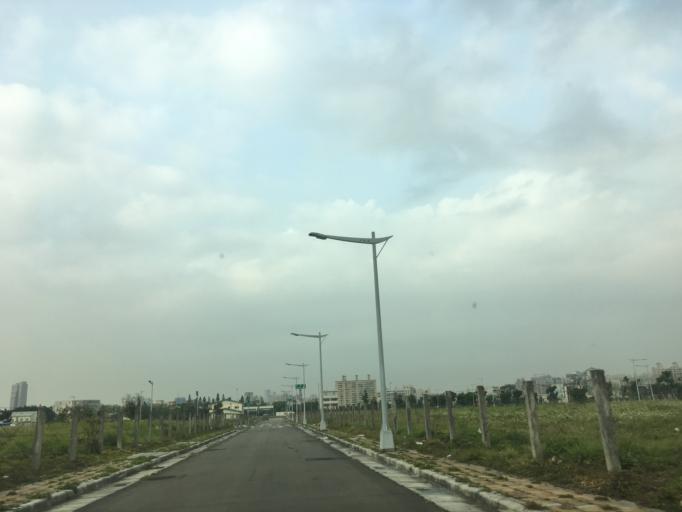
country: TW
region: Taiwan
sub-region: Taichung City
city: Taichung
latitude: 24.1890
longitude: 120.6786
